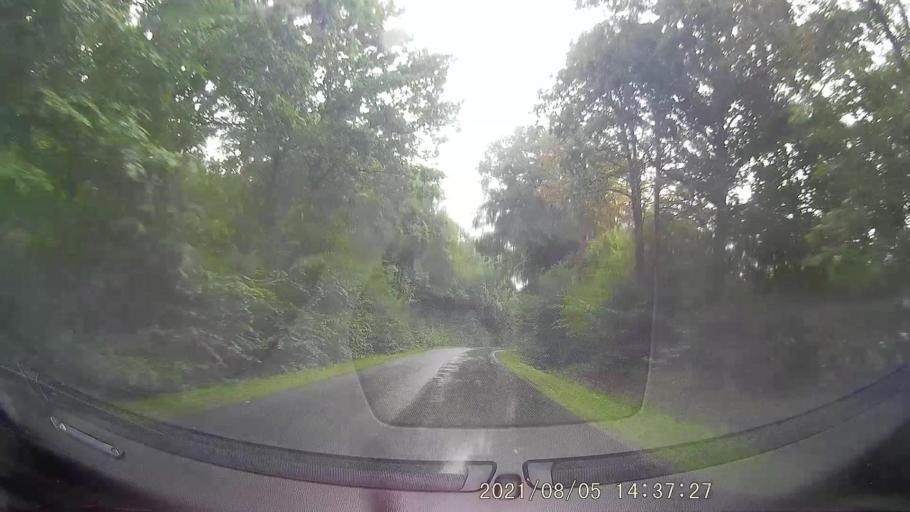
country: PL
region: Opole Voivodeship
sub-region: Powiat nyski
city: Sidzina
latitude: 50.4675
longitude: 17.4738
